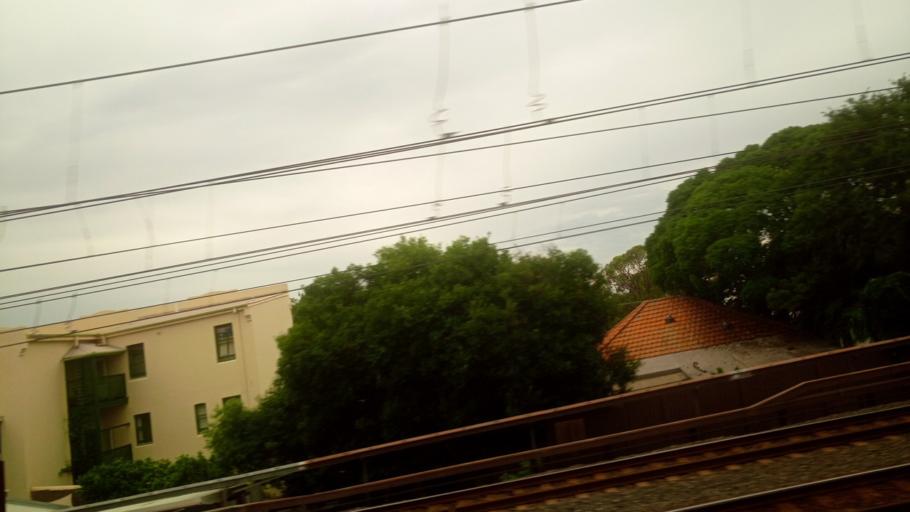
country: AU
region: New South Wales
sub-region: Marrickville
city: Newtown
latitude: -33.8974
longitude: 151.1841
